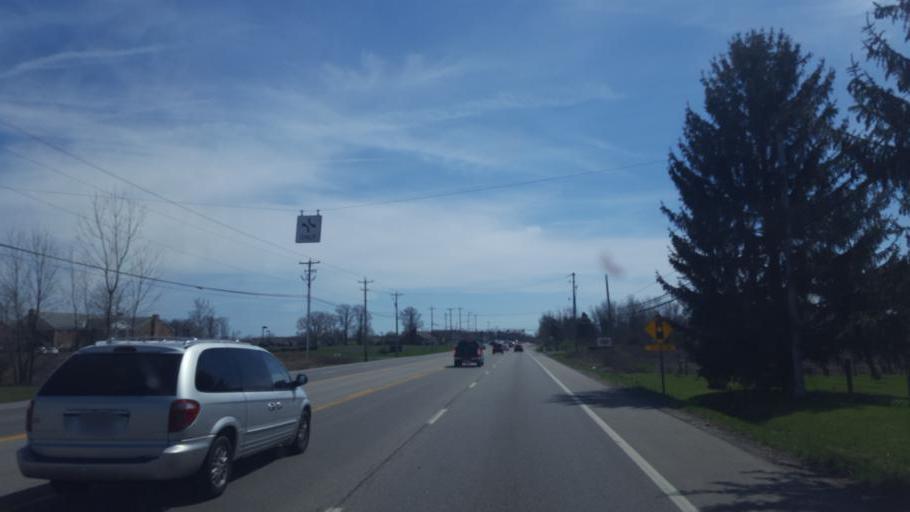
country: US
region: Ohio
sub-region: Delaware County
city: Lewis Center
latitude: 40.1778
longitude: -83.0227
